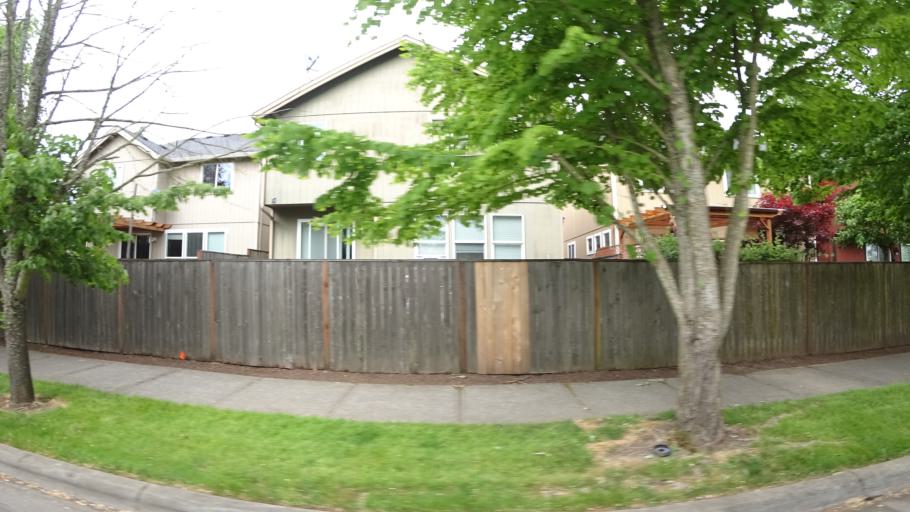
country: US
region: Oregon
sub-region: Washington County
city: Hillsboro
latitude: 45.4934
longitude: -122.9669
